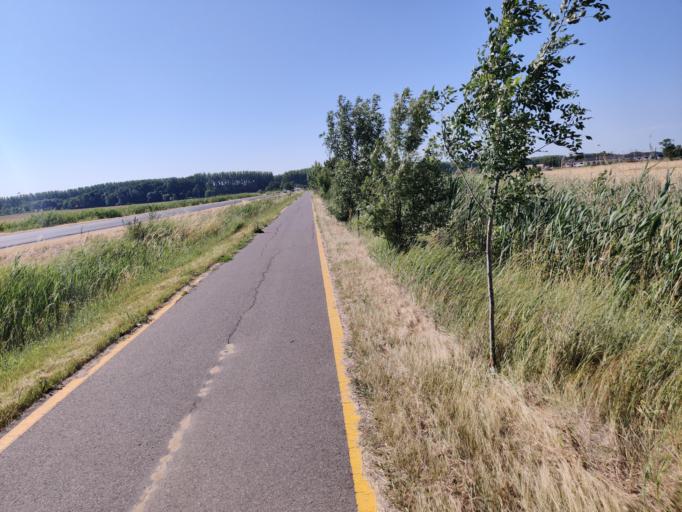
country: HU
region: Hajdu-Bihar
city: Balmazujvaros
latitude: 47.5893
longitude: 21.3437
